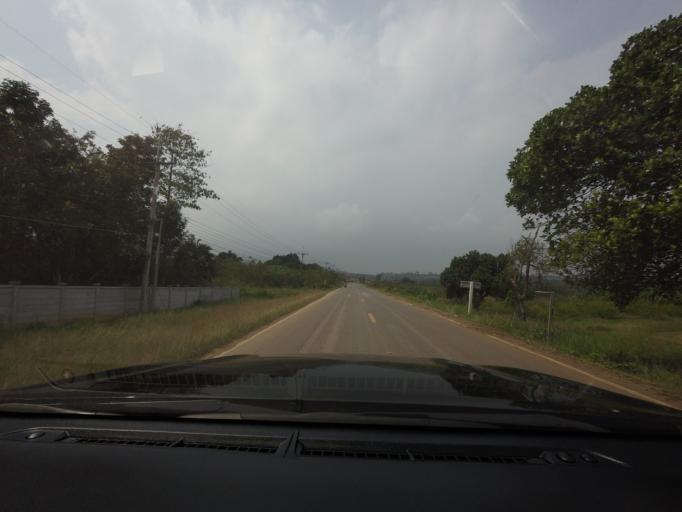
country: TH
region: Nakhon Ratchasima
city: Pak Chong
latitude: 14.4768
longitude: 101.5633
